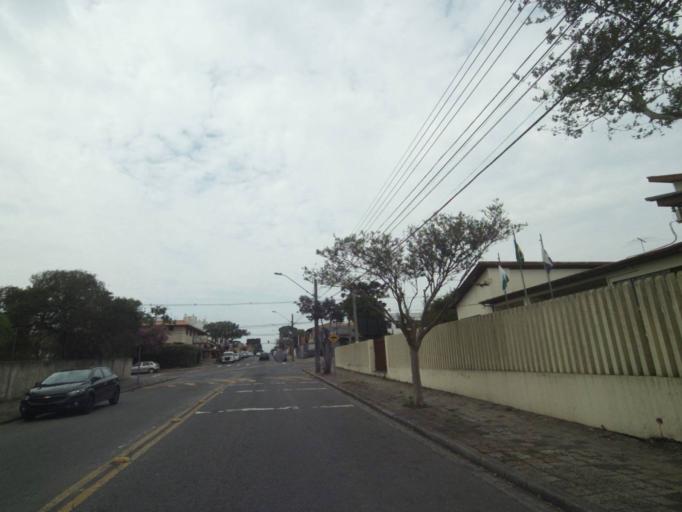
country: BR
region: Parana
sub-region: Curitiba
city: Curitiba
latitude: -25.4595
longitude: -49.3064
